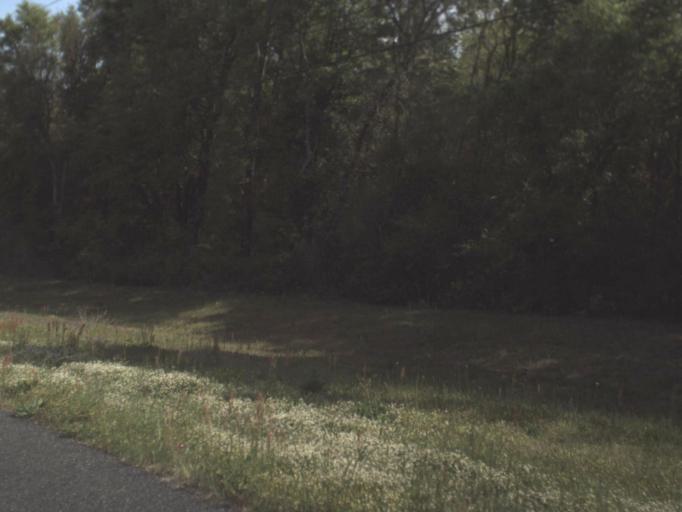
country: US
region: Florida
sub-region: Santa Rosa County
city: East Milton
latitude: 30.5990
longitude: -86.9448
